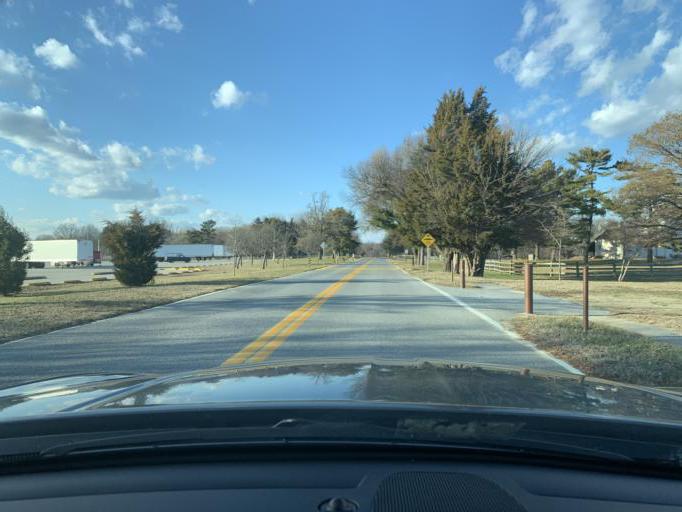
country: US
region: Maryland
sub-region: Anne Arundel County
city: Cape Saint Claire
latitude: 39.0134
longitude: -76.3990
